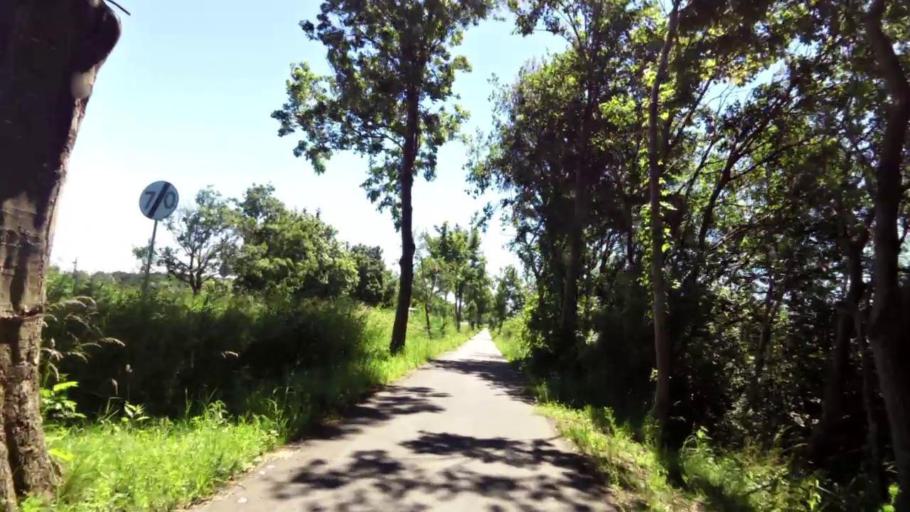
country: PL
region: West Pomeranian Voivodeship
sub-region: Powiat kolobrzeski
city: Kolobrzeg
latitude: 54.1351
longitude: 15.5594
